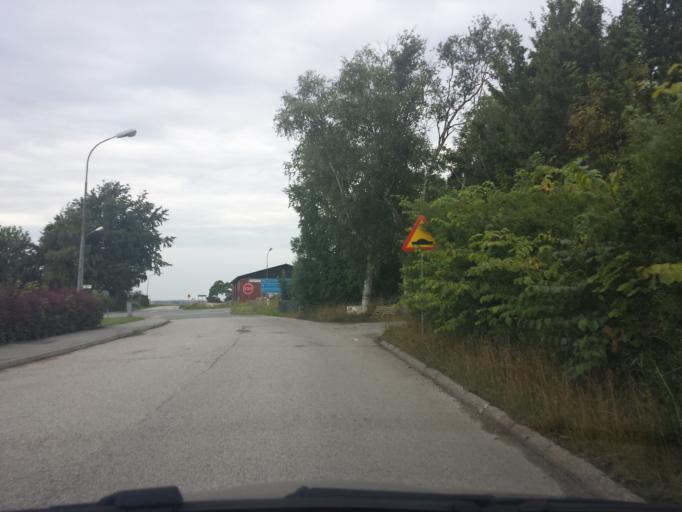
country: SE
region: Skane
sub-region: Ystads Kommun
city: Kopingebro
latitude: 55.4564
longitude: 14.0186
